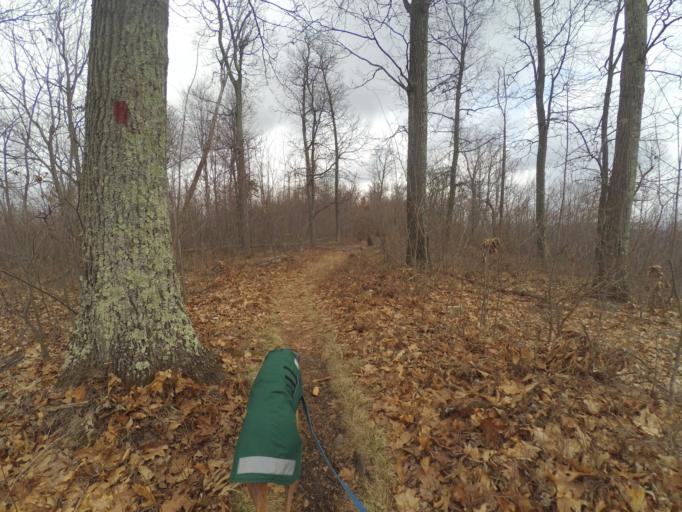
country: US
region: Pennsylvania
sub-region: Centre County
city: Boalsburg
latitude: 40.7605
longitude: -77.7190
